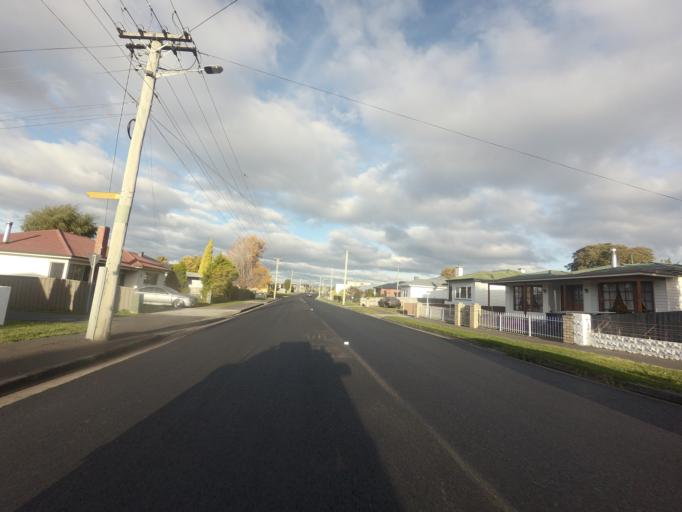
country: AU
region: Tasmania
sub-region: Glenorchy
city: Glenorchy
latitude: -42.8266
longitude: 147.2738
